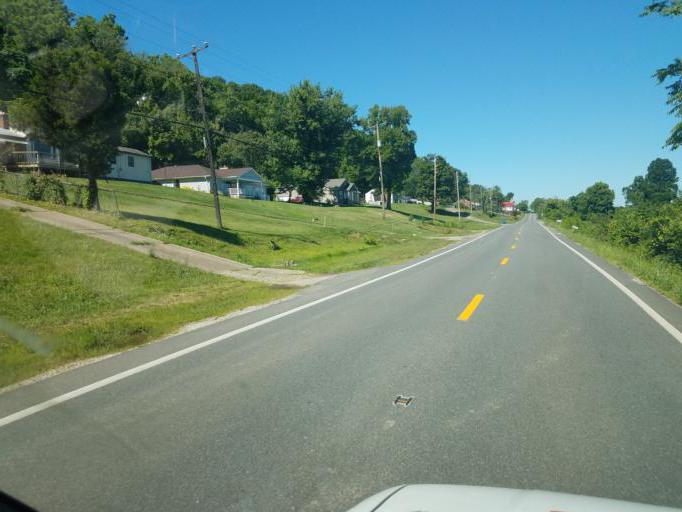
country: US
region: West Virginia
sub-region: Cabell County
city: Pea Ridge
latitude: 38.4366
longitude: -82.3441
